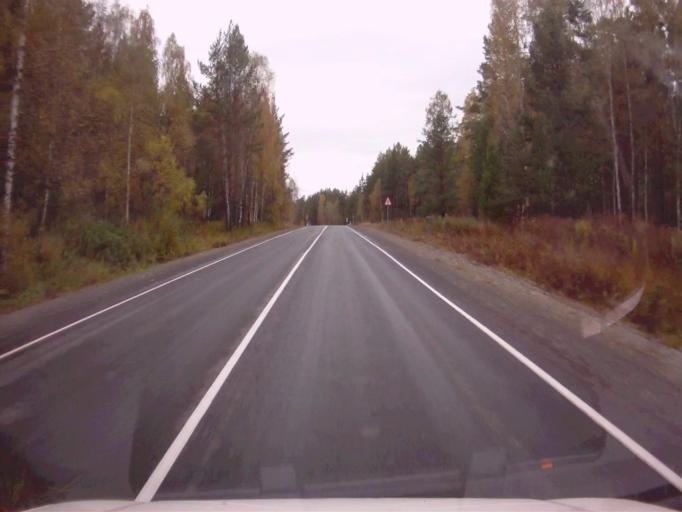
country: RU
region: Chelyabinsk
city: Nyazepetrovsk
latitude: 56.0595
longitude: 59.7316
